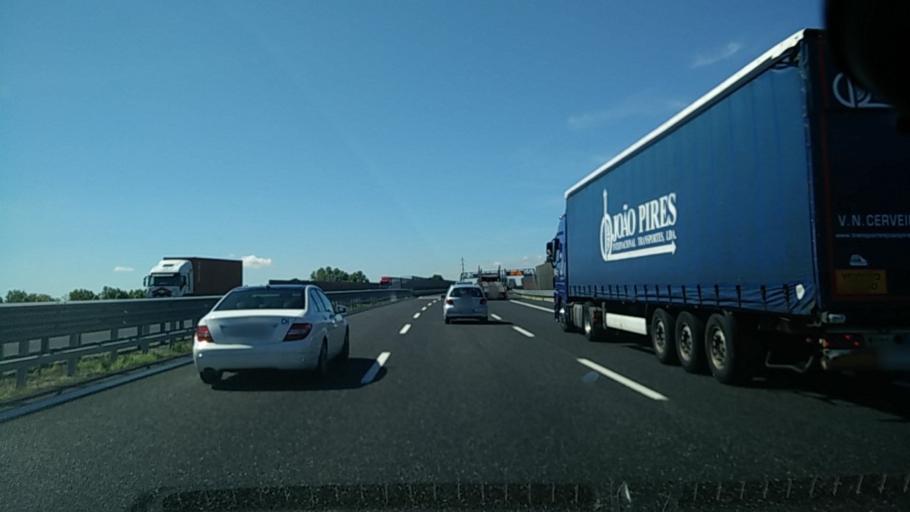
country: IT
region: Veneto
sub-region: Provincia di Venezia
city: Maerne
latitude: 45.5318
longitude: 12.1415
